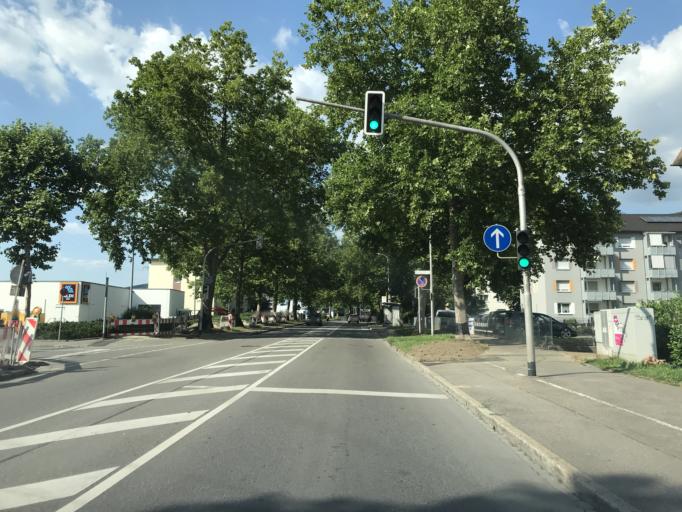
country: DE
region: Baden-Wuerttemberg
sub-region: Freiburg Region
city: Loerrach
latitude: 47.6245
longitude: 7.6767
